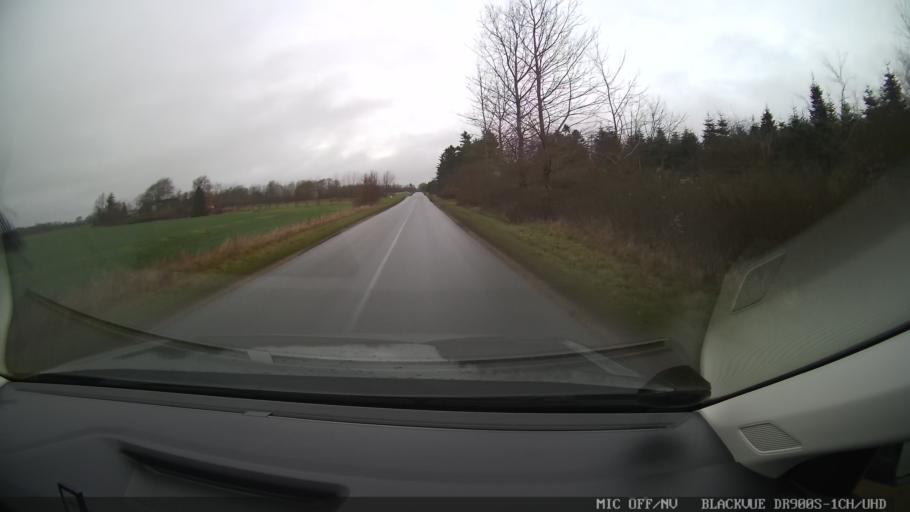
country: DK
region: Central Jutland
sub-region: Viborg Kommune
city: Karup
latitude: 56.3454
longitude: 9.2837
